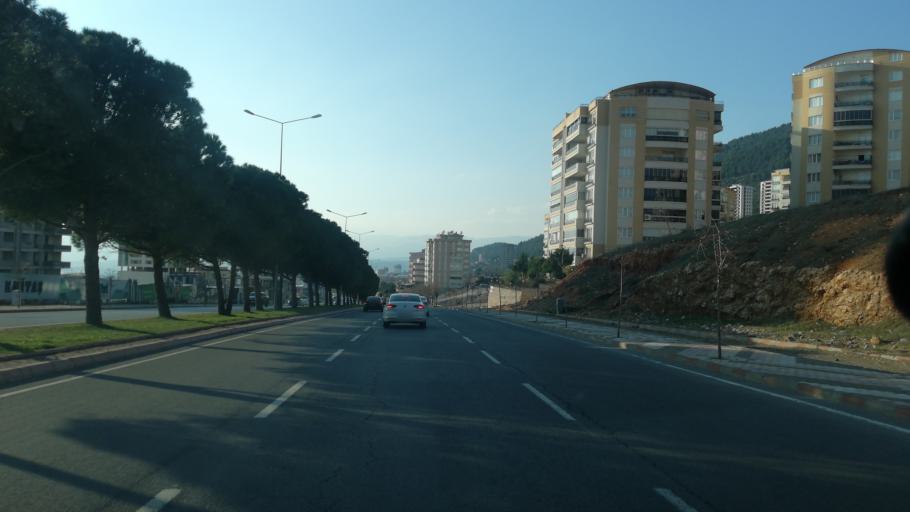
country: TR
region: Kahramanmaras
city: Kahramanmaras
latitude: 37.5965
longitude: 36.8495
